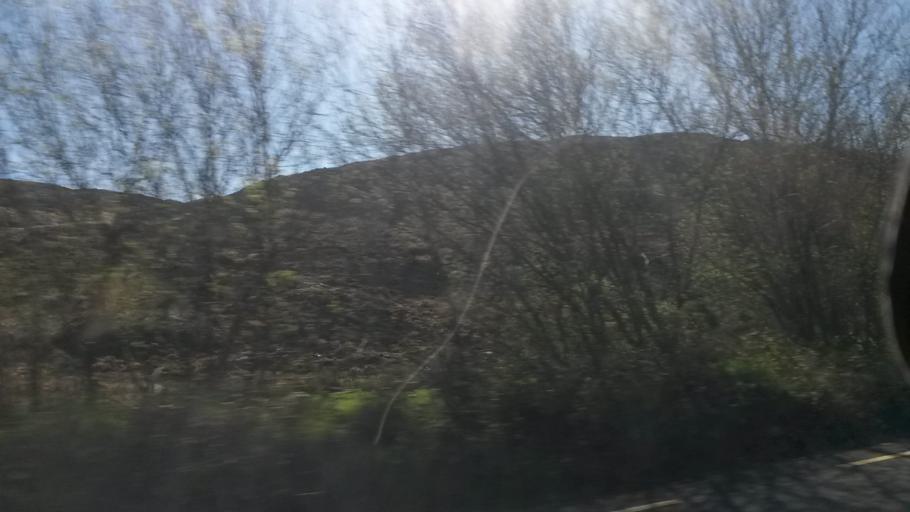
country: IE
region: Munster
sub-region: Ciarrai
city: Cill Airne
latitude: 51.9350
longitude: -9.3826
